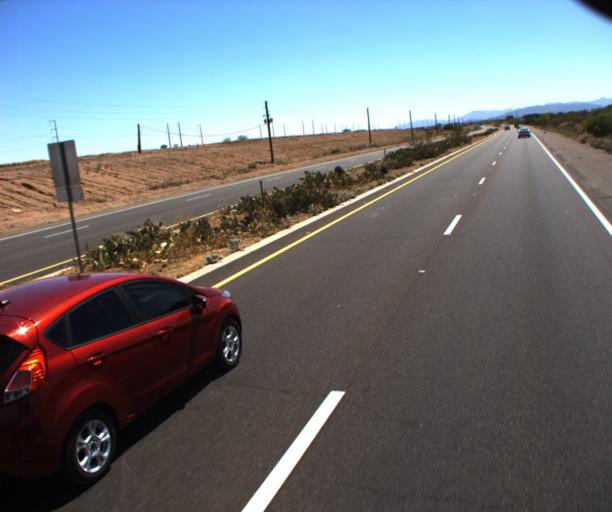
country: US
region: Arizona
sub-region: Maricopa County
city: Mesa
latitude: 33.4777
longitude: -111.8313
